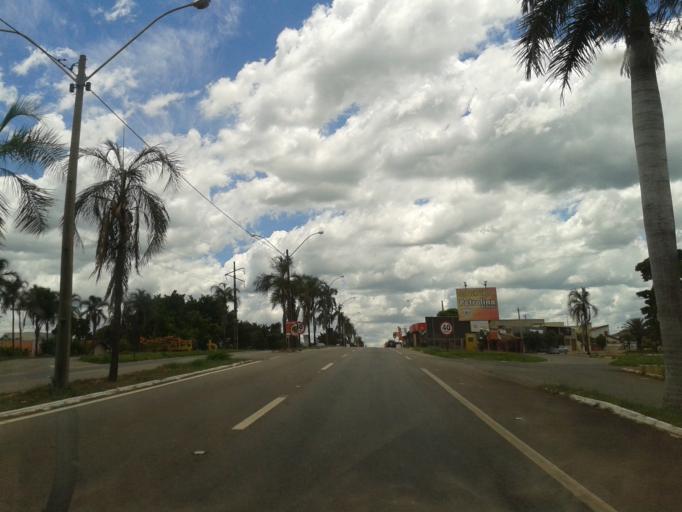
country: BR
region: Goias
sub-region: Petrolina De Goias
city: Petrolina de Goias
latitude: -16.1052
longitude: -49.3340
